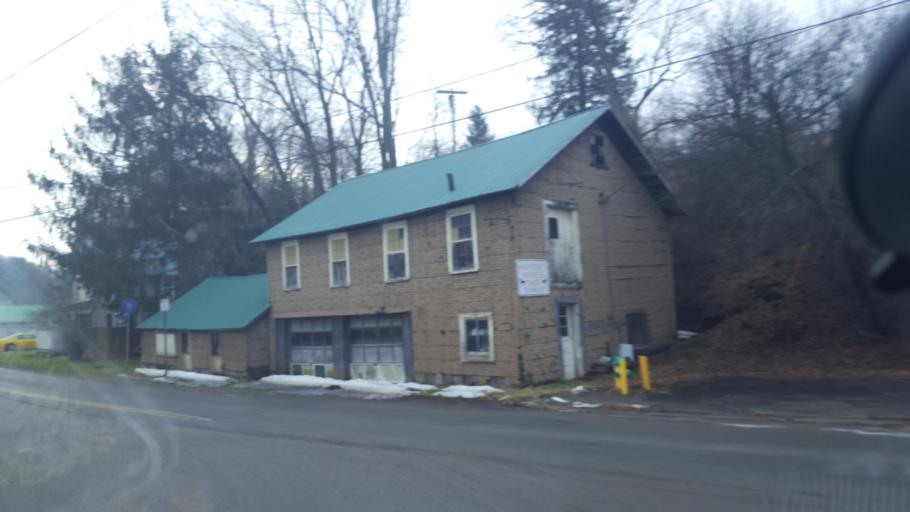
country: US
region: New York
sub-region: Allegany County
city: Andover
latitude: 42.0378
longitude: -77.7626
